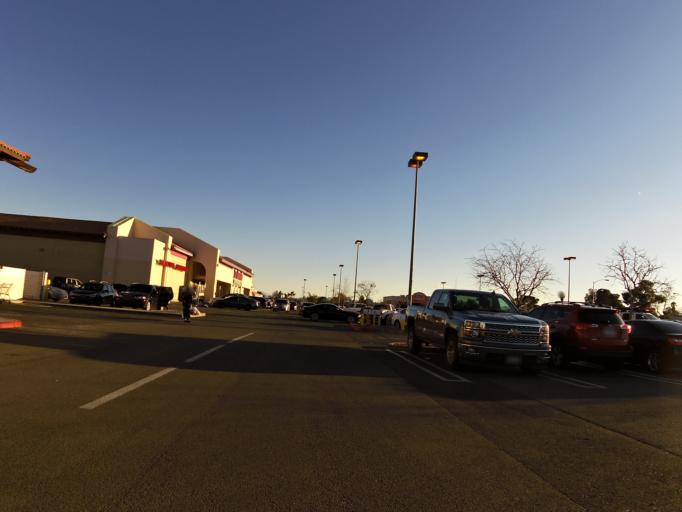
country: US
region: Nevada
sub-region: Clark County
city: Spring Valley
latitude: 36.1142
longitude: -115.2422
